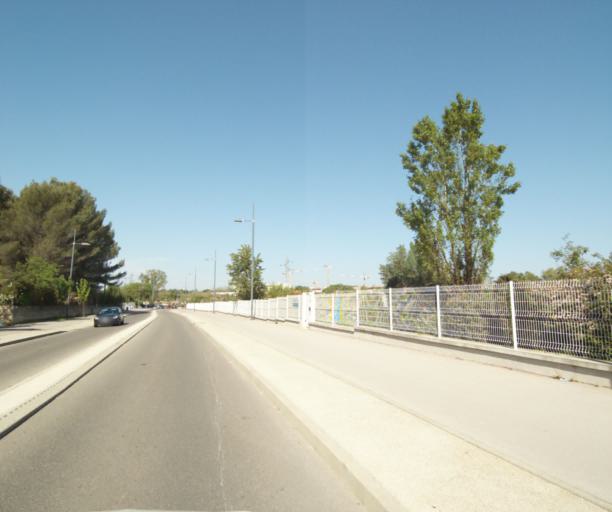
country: FR
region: Languedoc-Roussillon
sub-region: Departement de l'Herault
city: Castelnau-le-Lez
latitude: 43.6262
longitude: 3.9039
